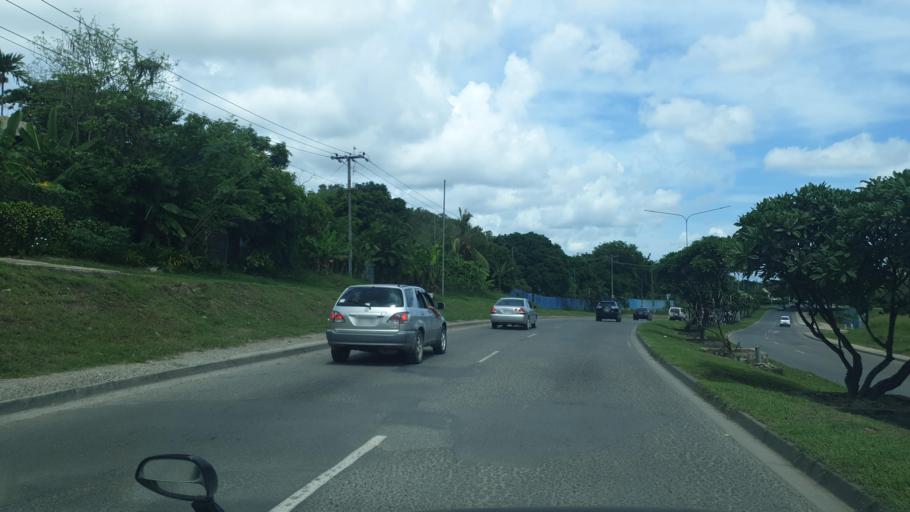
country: PG
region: National Capital
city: Port Moresby
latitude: -9.4209
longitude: 147.1770
